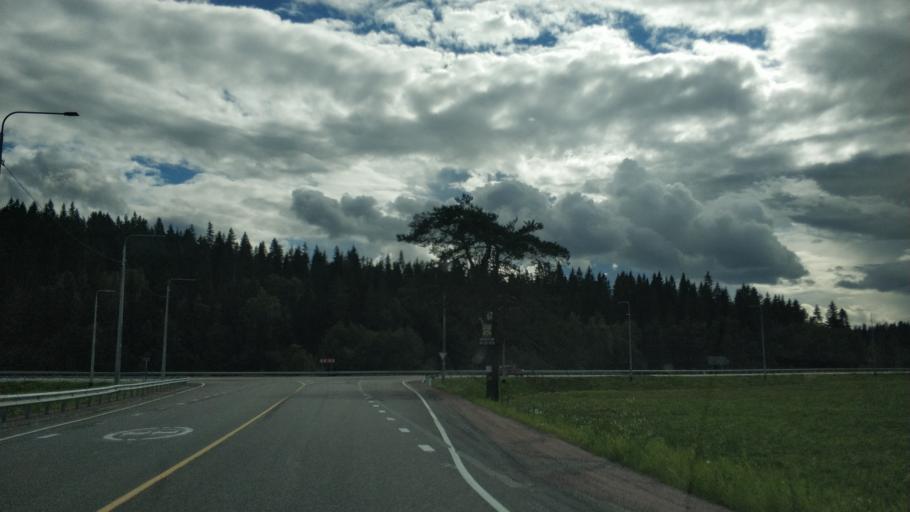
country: RU
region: Republic of Karelia
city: Khelyulya
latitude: 61.7766
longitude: 30.6614
